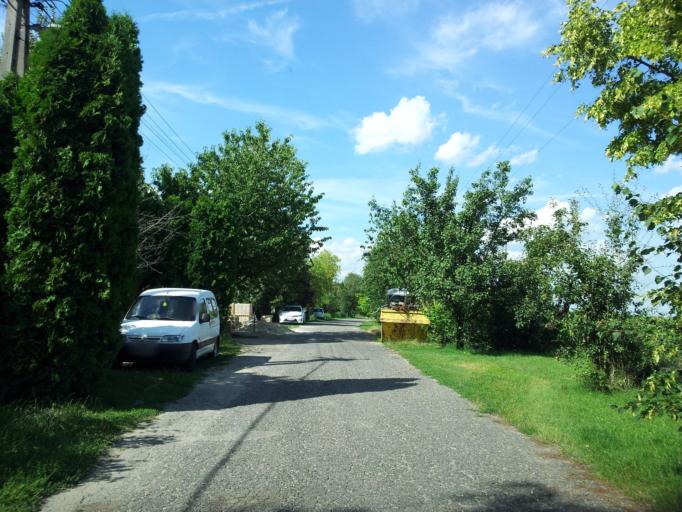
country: HU
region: Pest
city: Szigetcsep
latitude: 47.2493
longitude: 18.9801
